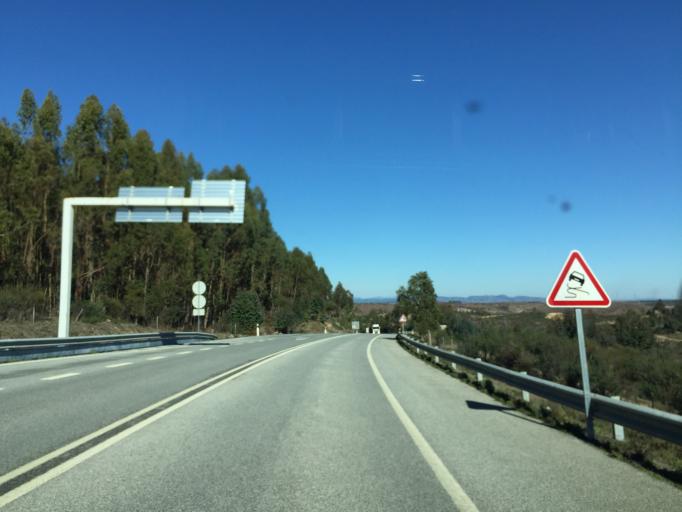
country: PT
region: Portalegre
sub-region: Nisa
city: Nisa
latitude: 39.4994
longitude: -7.7685
